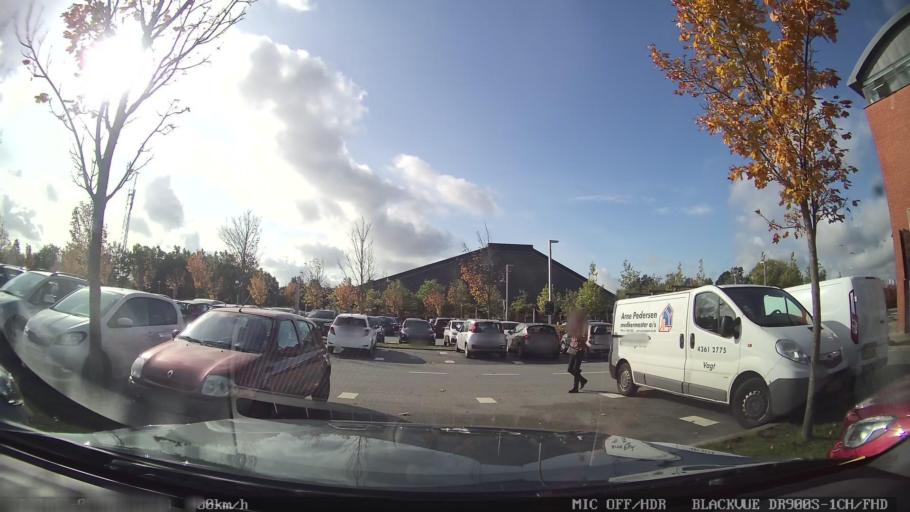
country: DK
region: Zealand
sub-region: Greve Kommune
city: Greve
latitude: 55.5816
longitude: 12.2935
